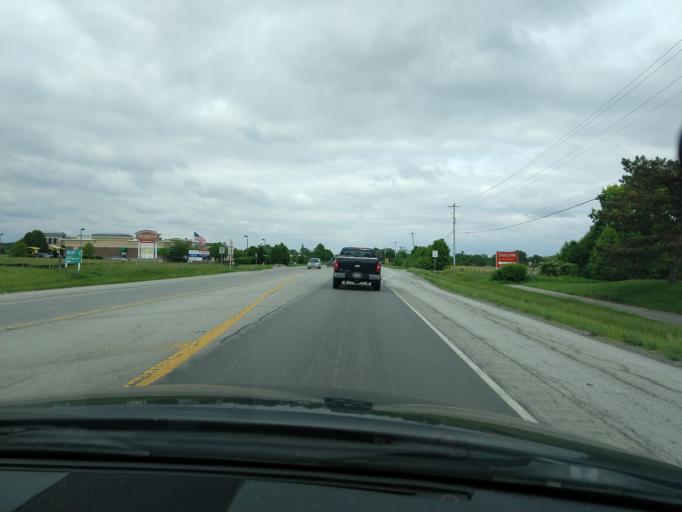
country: US
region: Indiana
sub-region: Hamilton County
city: Westfield
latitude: 40.0431
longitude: -86.0767
